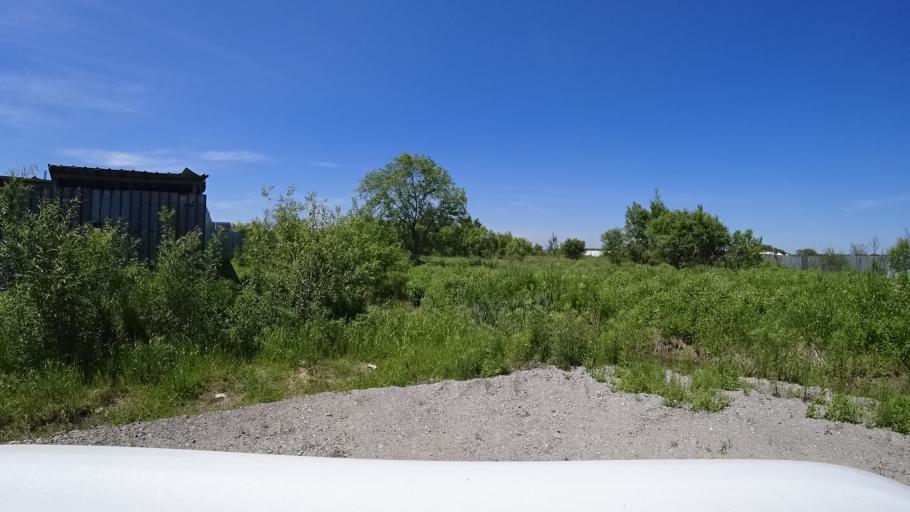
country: RU
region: Khabarovsk Krai
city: Topolevo
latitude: 48.5125
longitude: 135.1758
